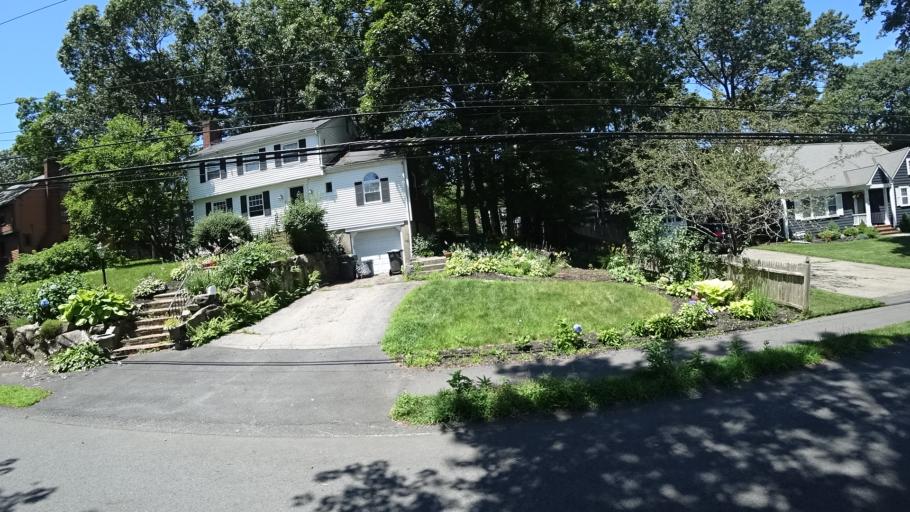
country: US
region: Massachusetts
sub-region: Norfolk County
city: Dedham
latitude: 42.2199
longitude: -71.1581
